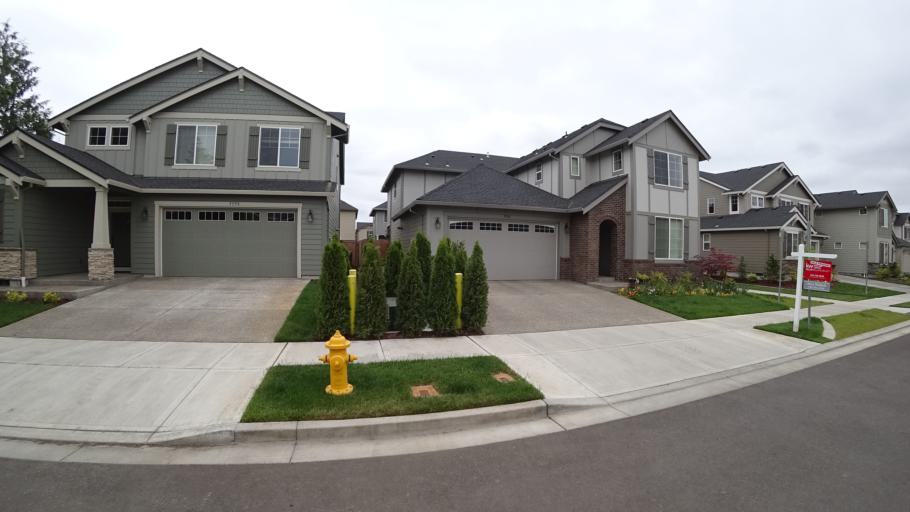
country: US
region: Oregon
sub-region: Washington County
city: Aloha
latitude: 45.4954
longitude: -122.9254
